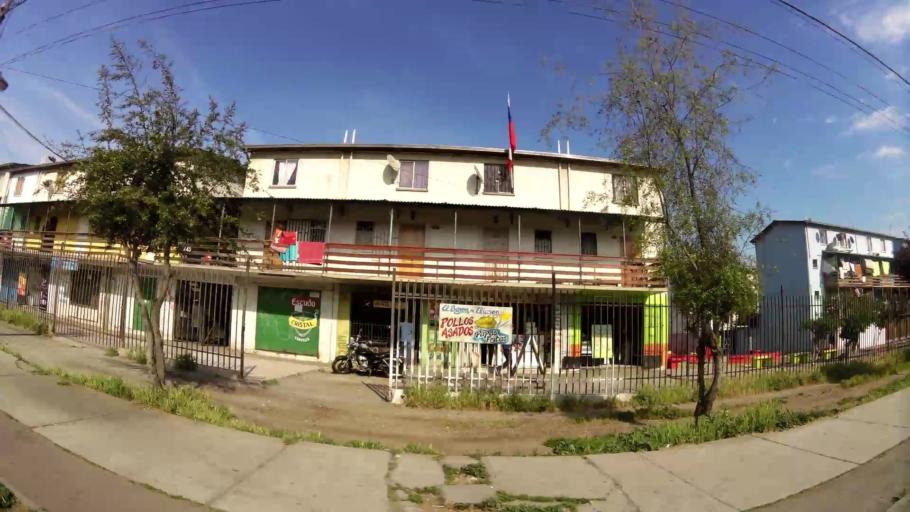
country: CL
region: Santiago Metropolitan
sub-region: Provincia de Santiago
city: La Pintana
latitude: -33.5574
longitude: -70.6314
